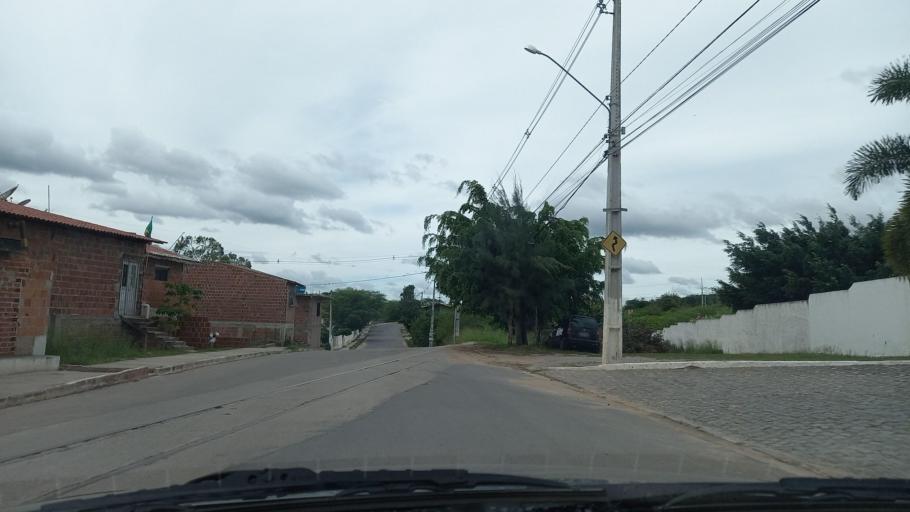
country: BR
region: Pernambuco
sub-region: Gravata
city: Gravata
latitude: -8.2112
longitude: -35.5987
